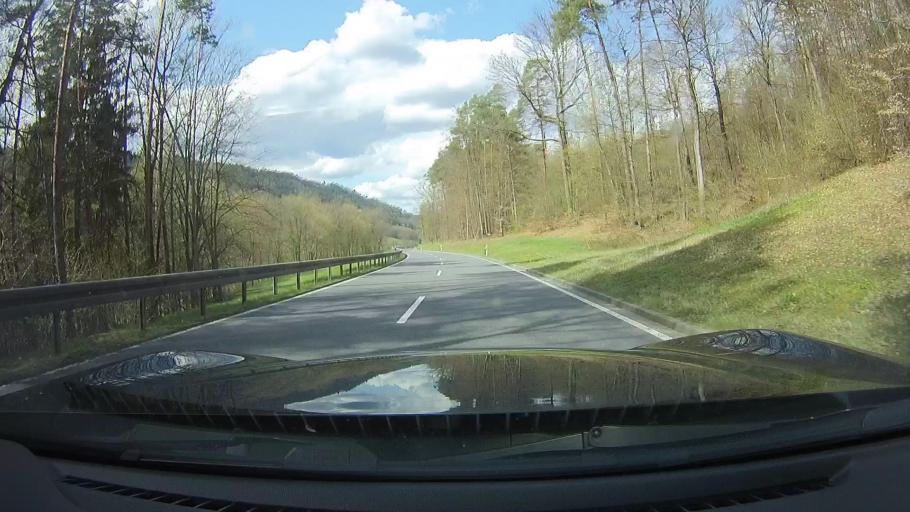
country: DE
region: Bavaria
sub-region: Regierungsbezirk Unterfranken
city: Kirchzell
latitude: 49.5989
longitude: 9.2036
